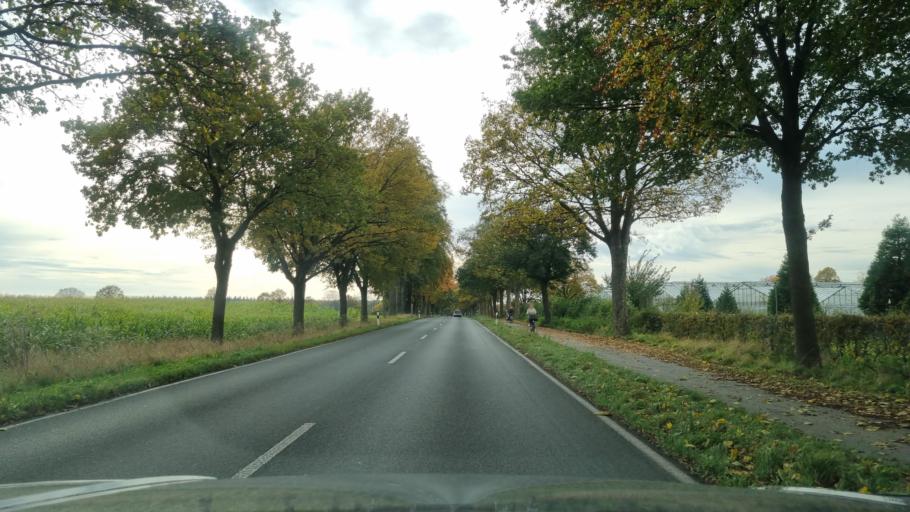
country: DE
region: North Rhine-Westphalia
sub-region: Regierungsbezirk Dusseldorf
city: Kleve
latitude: 51.7571
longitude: 6.1018
